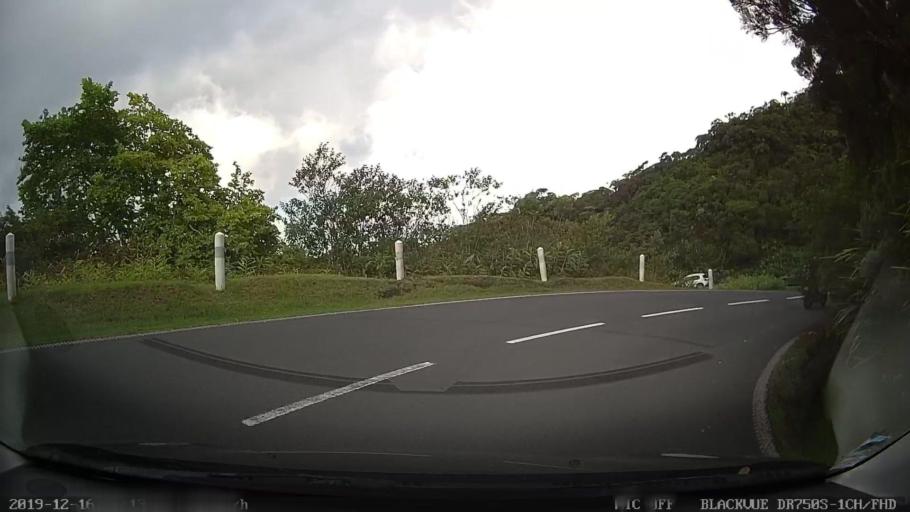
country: RE
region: Reunion
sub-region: Reunion
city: Cilaos
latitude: -21.1608
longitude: 55.5957
